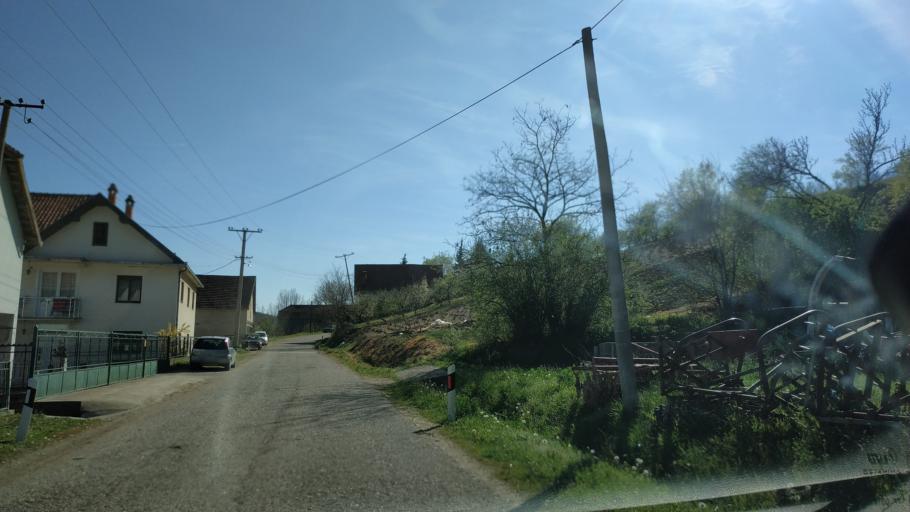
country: RS
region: Central Serbia
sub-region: Nisavski Okrug
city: Aleksinac
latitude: 43.4861
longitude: 21.6591
